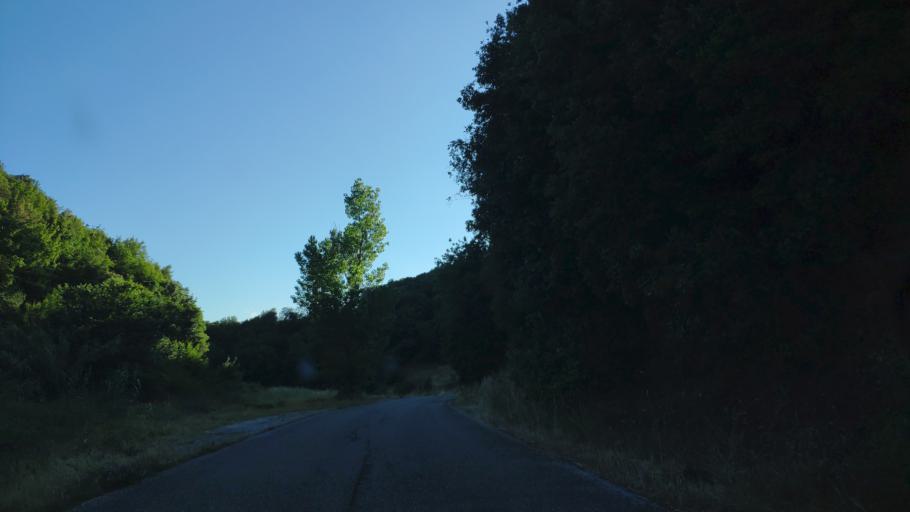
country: GR
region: West Greece
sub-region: Nomos Aitolias kai Akarnanias
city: Fitiai
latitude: 38.6370
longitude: 21.1722
